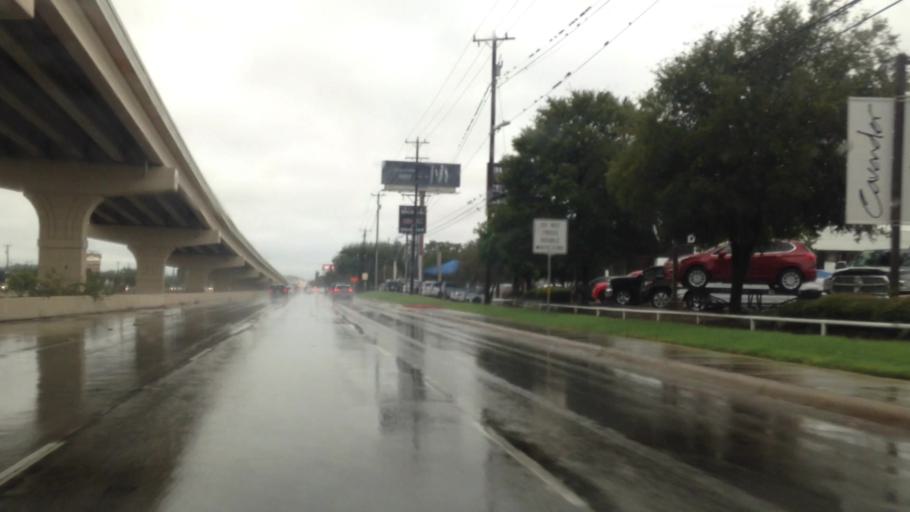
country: US
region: Texas
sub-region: Bexar County
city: Hollywood Park
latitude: 29.6060
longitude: -98.4699
